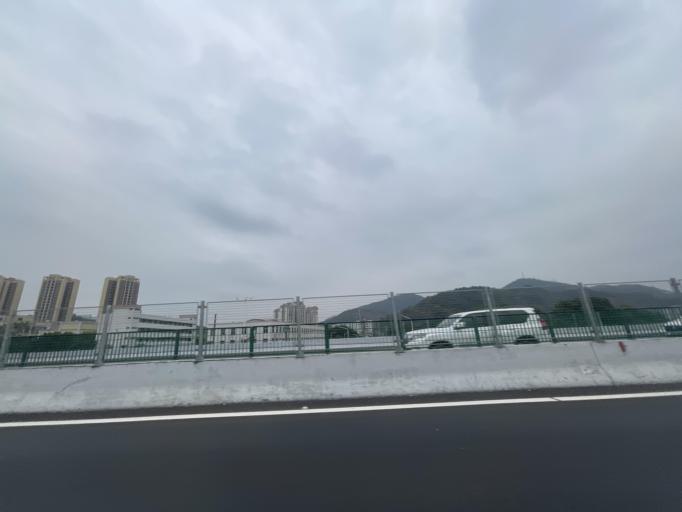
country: CN
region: Guangdong
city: Nansha
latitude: 22.7791
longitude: 113.5401
